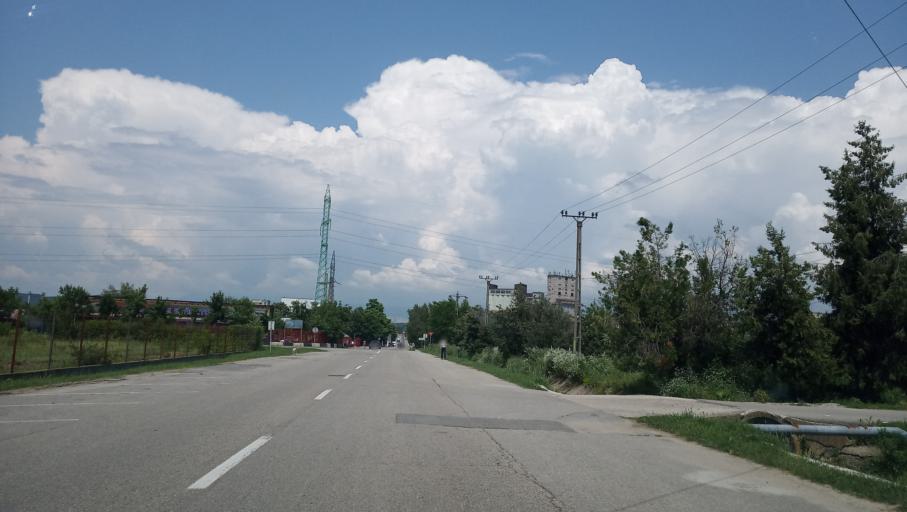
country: RO
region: Gorj
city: Targu Jiu
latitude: 45.0679
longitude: 23.3114
